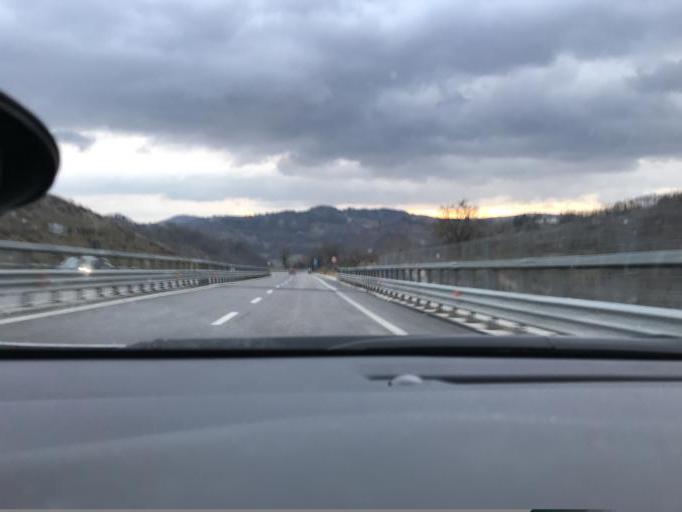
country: IT
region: Umbria
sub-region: Provincia di Perugia
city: Valfabbrica
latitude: 43.1827
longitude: 12.6191
